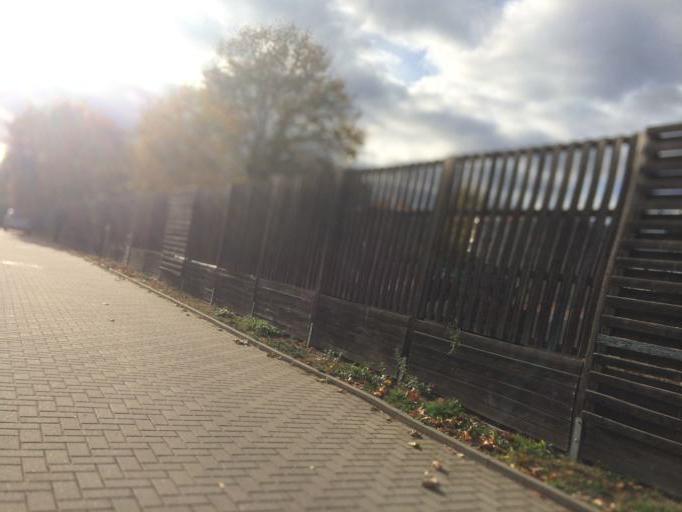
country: DE
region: Berlin
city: Rosenthal
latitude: 52.5978
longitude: 13.3778
